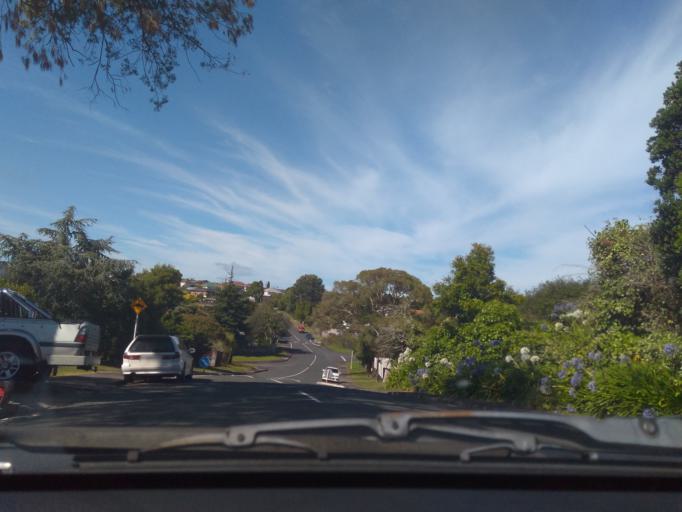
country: NZ
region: Auckland
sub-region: Auckland
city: Waitakere
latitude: -36.8962
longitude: 174.6414
